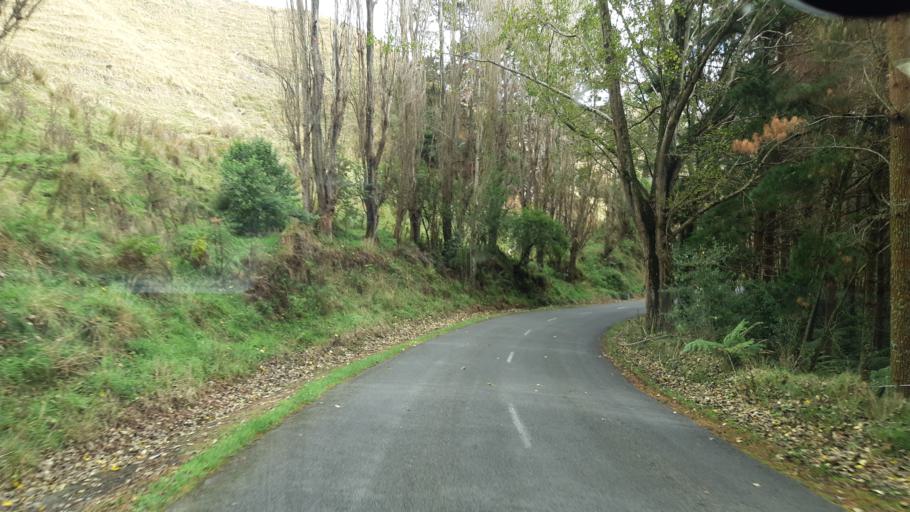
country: NZ
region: Manawatu-Wanganui
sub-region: Rangitikei District
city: Bulls
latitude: -39.9111
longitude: 175.5485
